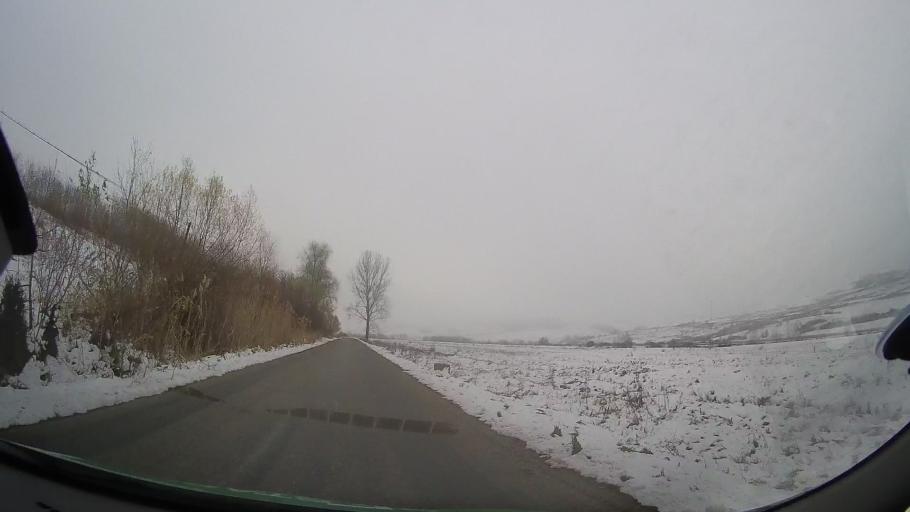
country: RO
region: Bacau
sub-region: Comuna Vultureni
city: Vultureni
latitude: 46.3113
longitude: 27.2926
